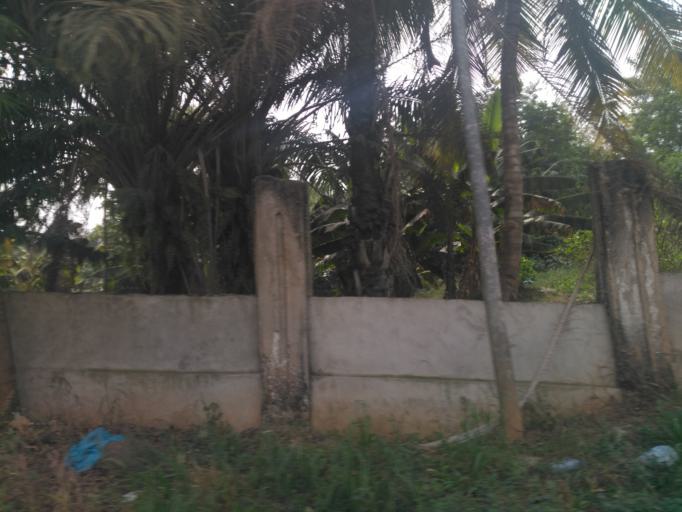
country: GH
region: Ashanti
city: Kumasi
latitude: 6.6791
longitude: -1.6212
